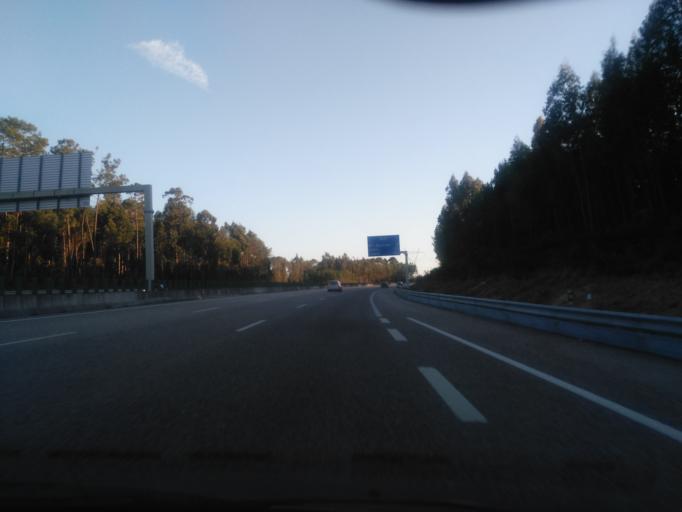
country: PT
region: Leiria
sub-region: Pombal
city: Lourical
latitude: 39.9403
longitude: -8.7702
